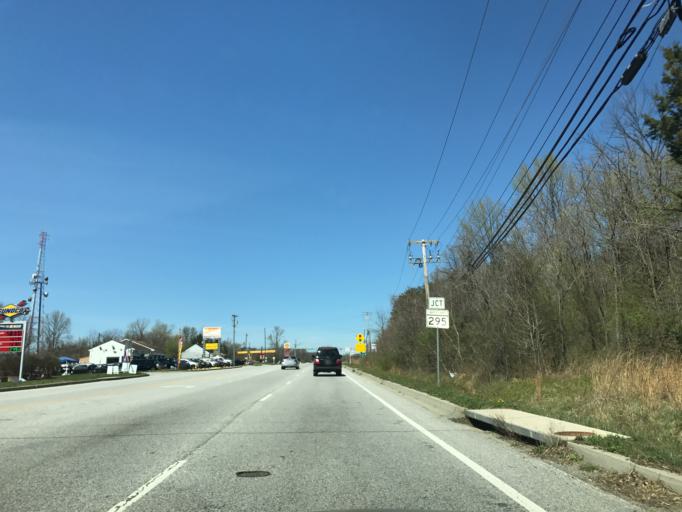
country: US
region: Maryland
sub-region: Anne Arundel County
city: Jessup
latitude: 39.1369
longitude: -76.7499
